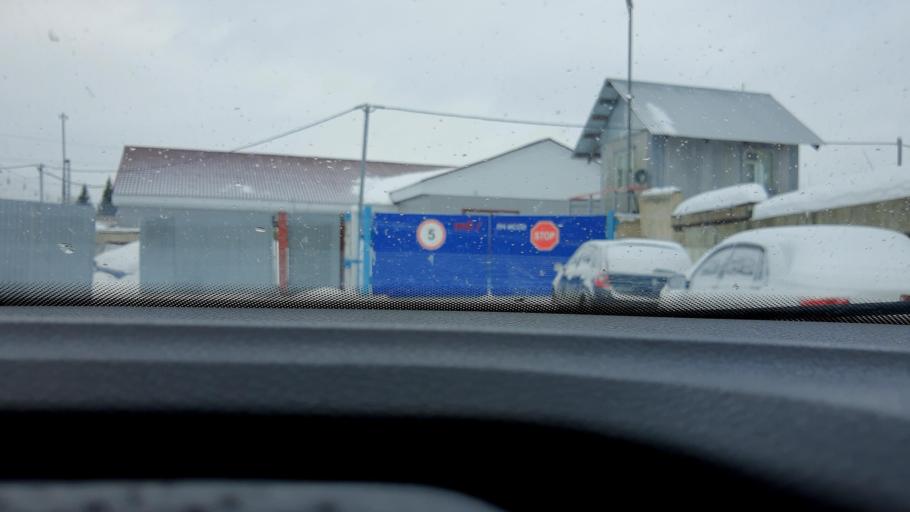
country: RU
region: Bashkortostan
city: Mikhaylovka
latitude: 54.6944
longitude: 55.8430
